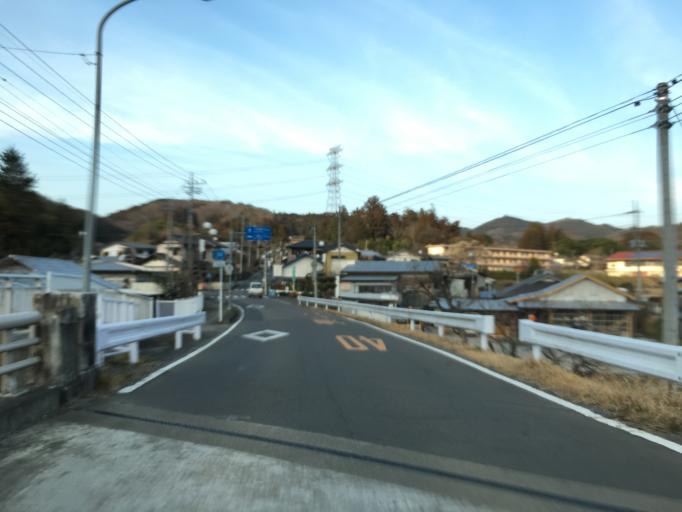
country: JP
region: Ibaraki
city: Daigo
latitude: 36.8153
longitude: 140.3701
